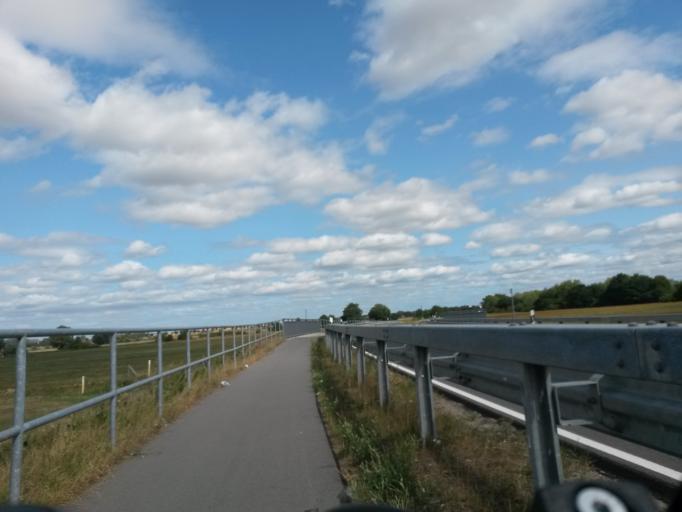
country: DE
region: Saxony-Anhalt
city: Tangermunde
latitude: 52.5147
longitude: 11.9270
